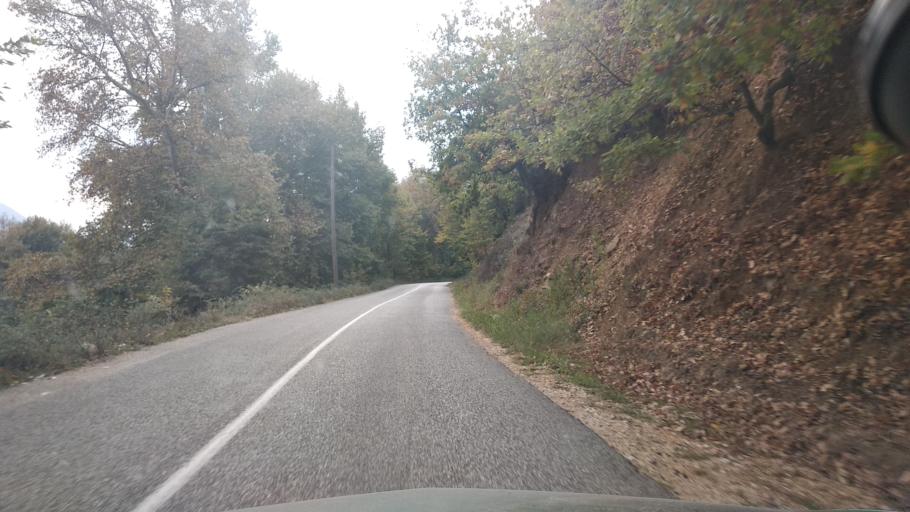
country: GR
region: Thessaly
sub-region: Trikala
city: Kastraki
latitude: 39.6895
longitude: 21.5172
